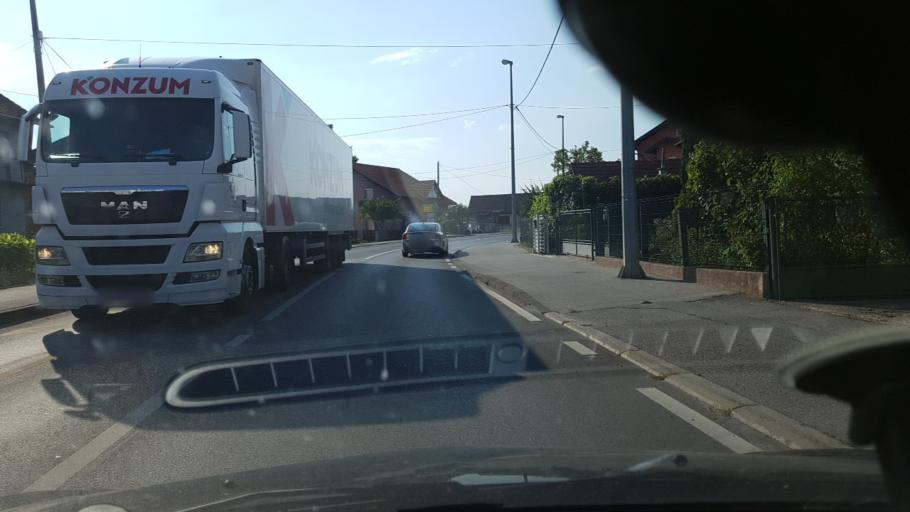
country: HR
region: Zagrebacka
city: Zapresic
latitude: 45.8612
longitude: 15.7960
